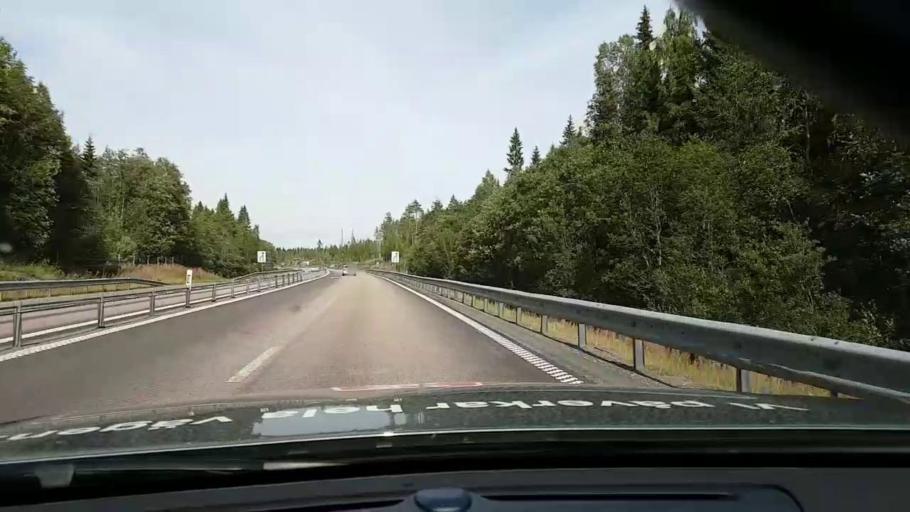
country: SE
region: Vaesternorrland
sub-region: OErnskoeldsviks Kommun
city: Husum
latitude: 63.4295
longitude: 19.2084
